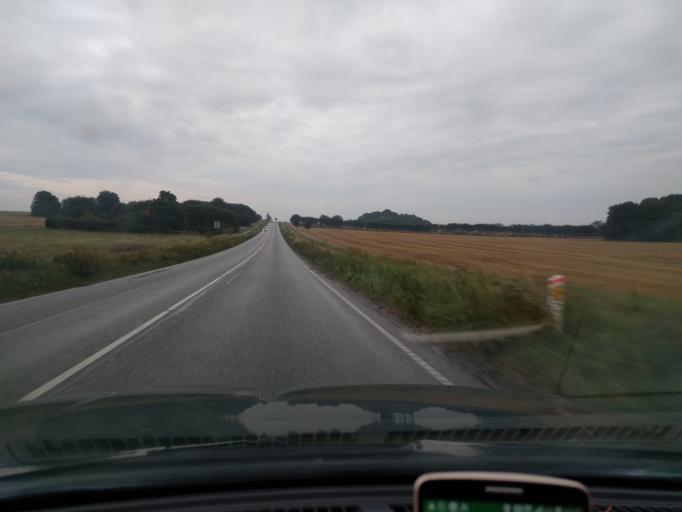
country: DK
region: Zealand
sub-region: Naestved Kommune
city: Naestved
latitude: 55.1701
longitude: 11.8107
